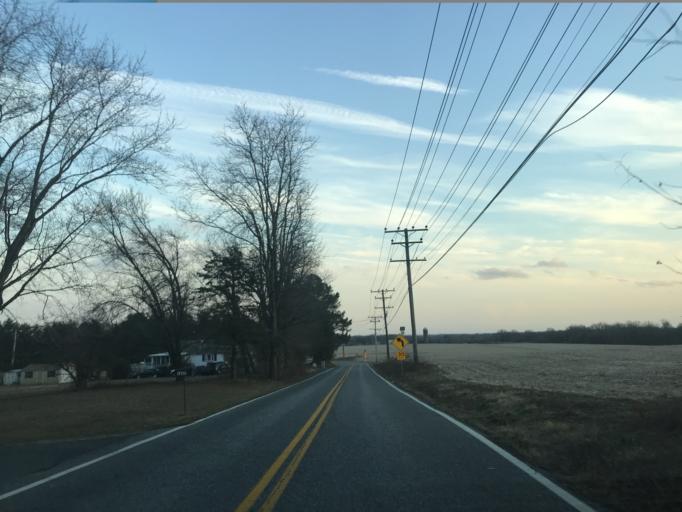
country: US
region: Maryland
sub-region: Harford County
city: Bel Air South
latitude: 39.5233
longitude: -76.2763
